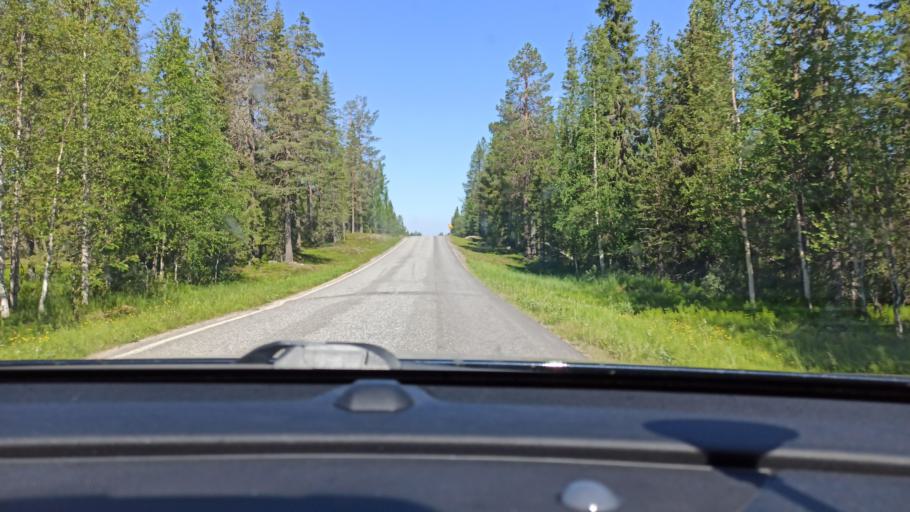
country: FI
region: Lapland
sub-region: Tunturi-Lappi
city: Kolari
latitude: 67.6744
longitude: 24.1454
